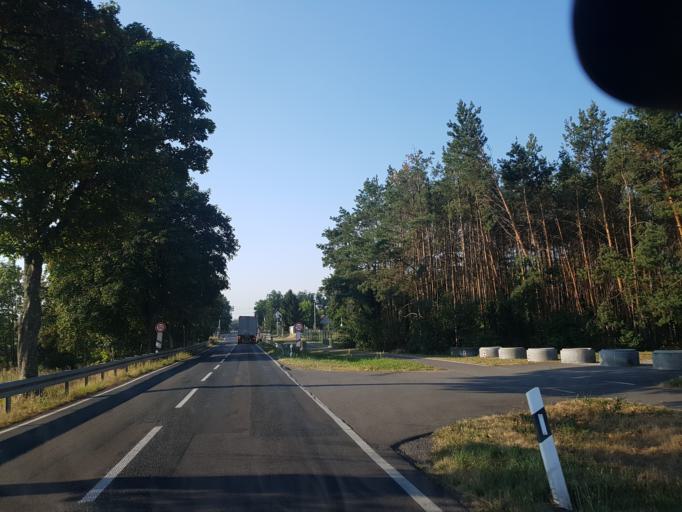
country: DE
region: Brandenburg
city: Hohenleipisch
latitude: 51.4831
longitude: 13.5470
